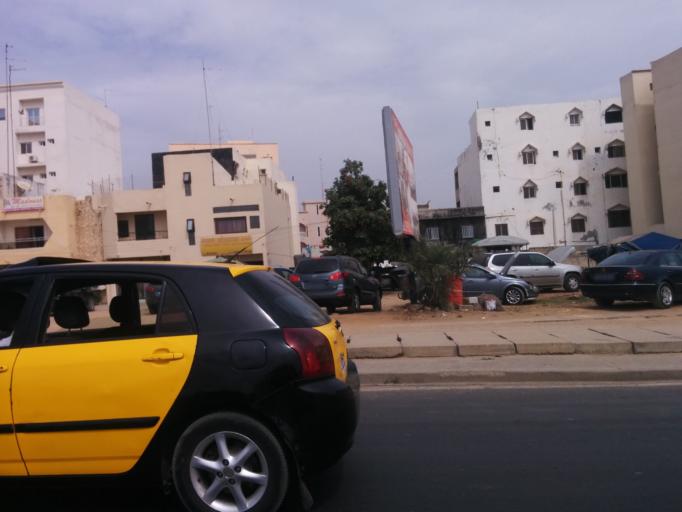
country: SN
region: Dakar
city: Mermoz Boabab
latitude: 14.7303
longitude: -17.4727
